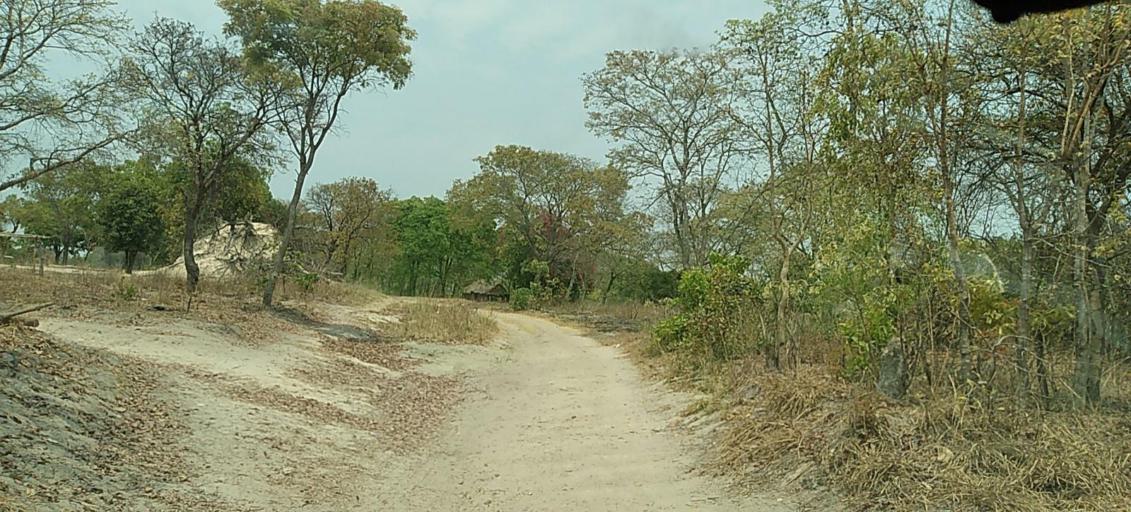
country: ZM
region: North-Western
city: Kabompo
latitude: -13.5401
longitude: 24.4524
